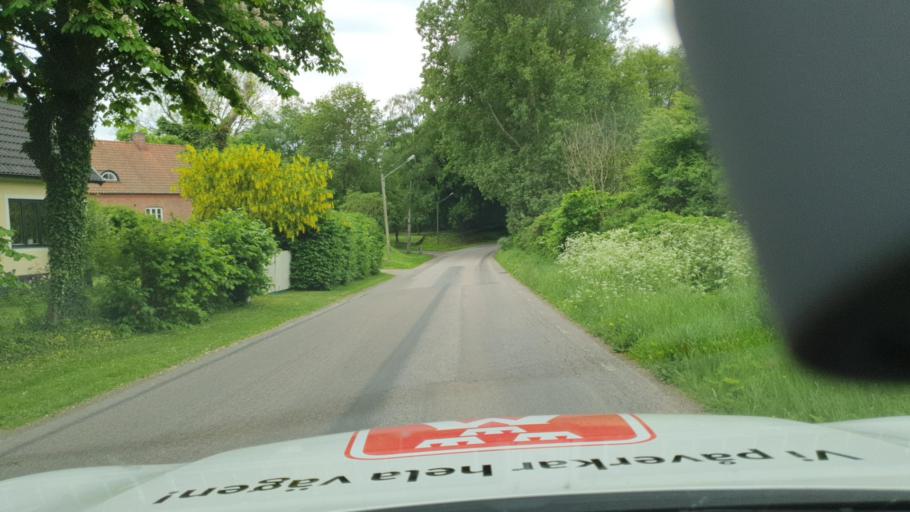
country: SE
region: Skane
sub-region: Tomelilla Kommun
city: Tomelilla
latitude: 55.5061
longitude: 13.9534
